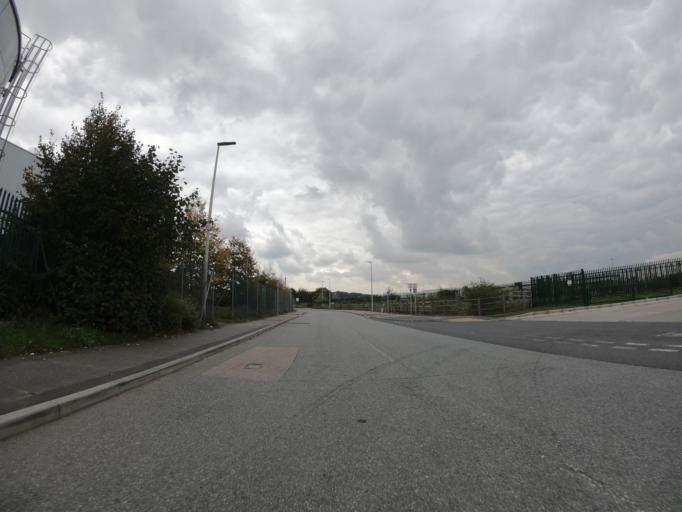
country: GB
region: England
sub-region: Greater London
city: Erith
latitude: 51.4953
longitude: 0.1685
